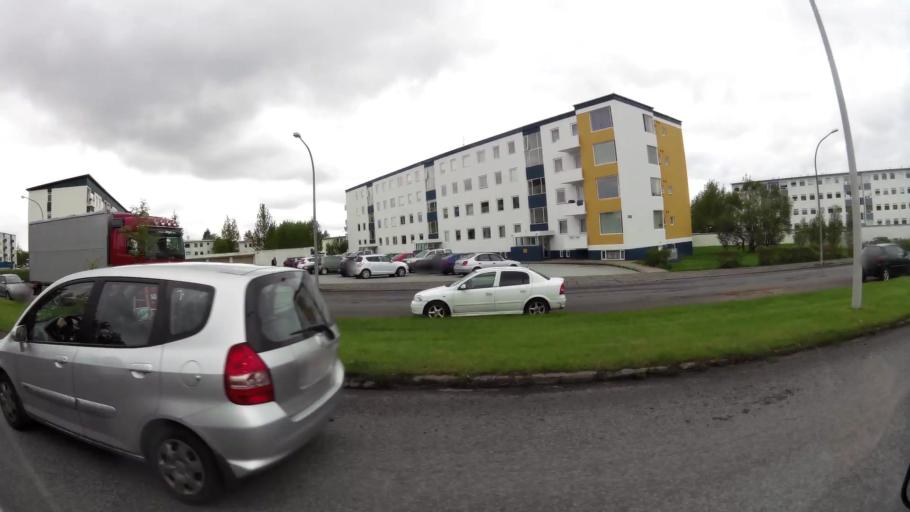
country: IS
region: Capital Region
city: Reykjavik
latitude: 64.1361
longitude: -21.8864
